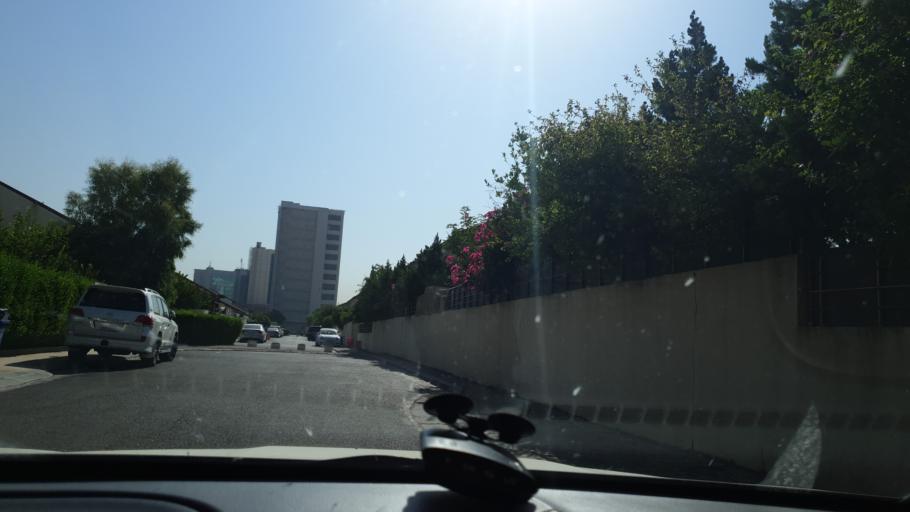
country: IQ
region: Arbil
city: Erbil
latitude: 36.1861
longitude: 43.9677
